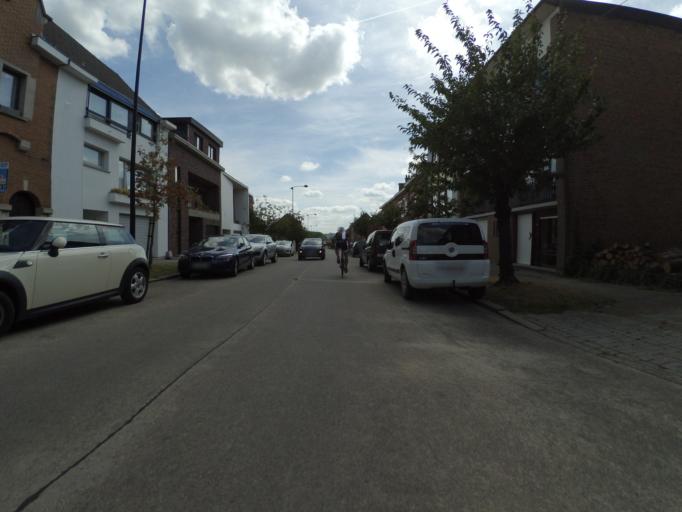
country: BE
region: Flanders
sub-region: Provincie Oost-Vlaanderen
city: Ronse
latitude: 50.7389
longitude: 3.5984
